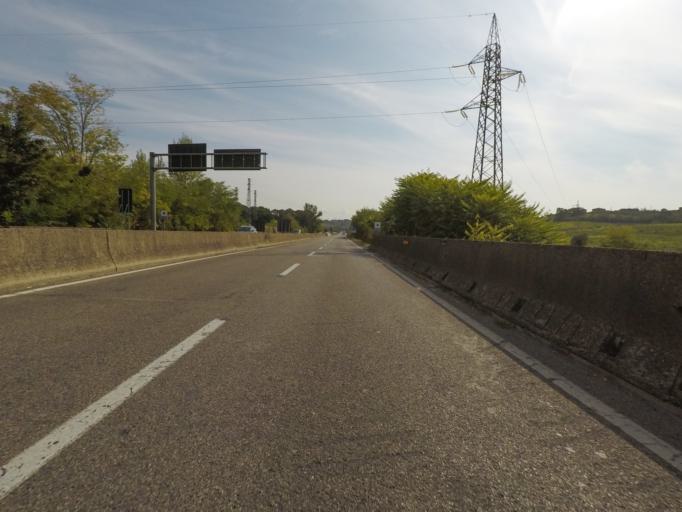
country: IT
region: Tuscany
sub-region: Provincia di Siena
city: Siena
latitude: 43.2988
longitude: 11.3281
